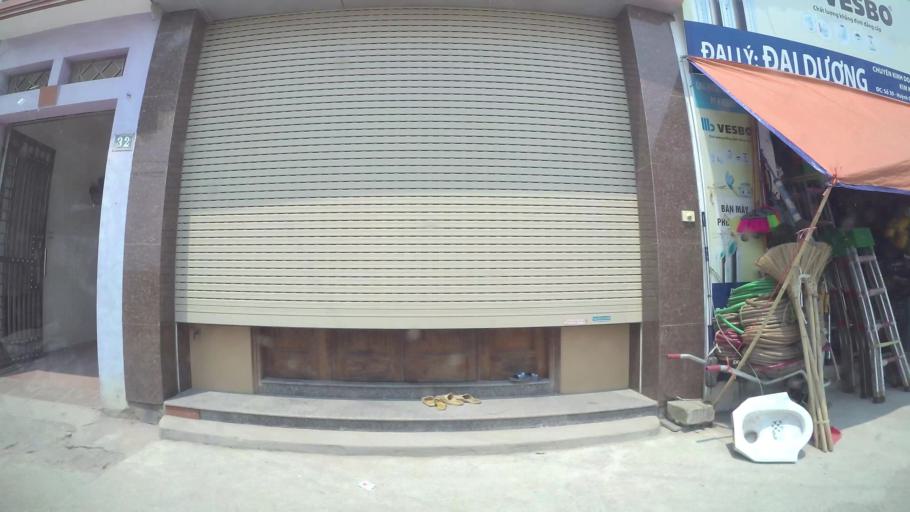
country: VN
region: Ha Noi
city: Van Dien
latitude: 20.9510
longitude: 105.8301
